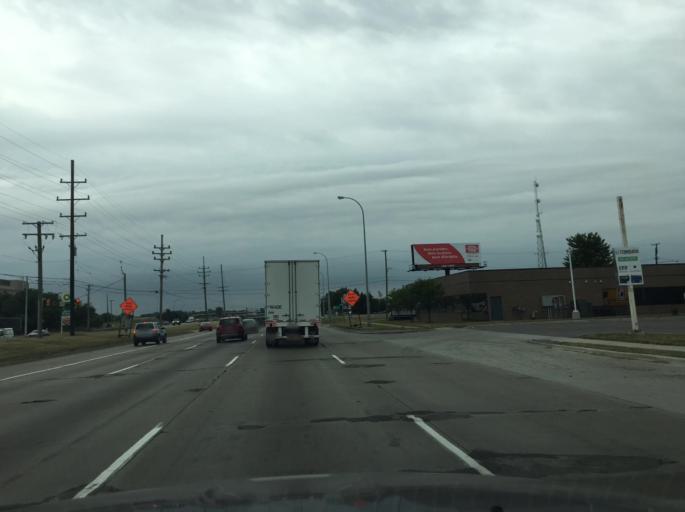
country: US
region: Michigan
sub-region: Macomb County
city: Center Line
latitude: 42.4982
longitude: -83.0465
